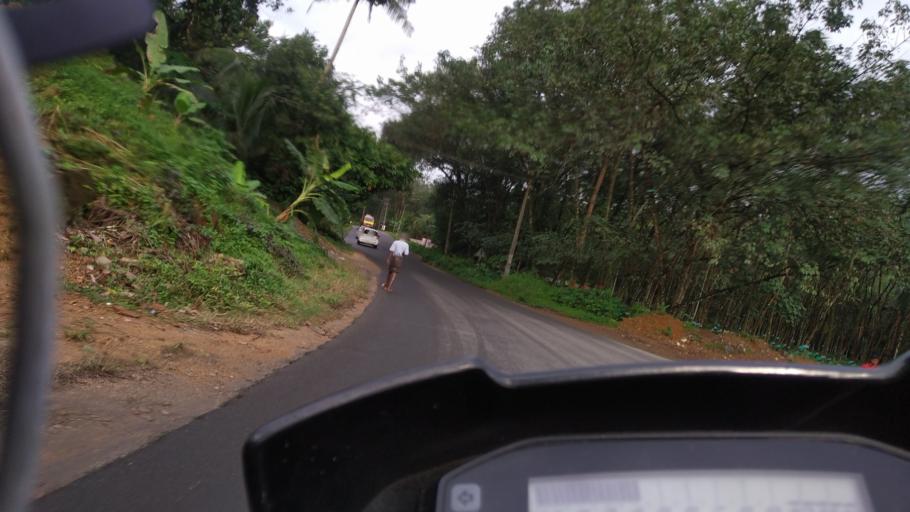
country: IN
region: Kerala
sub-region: Idukki
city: Kuttampuzha
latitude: 10.0500
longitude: 76.7274
